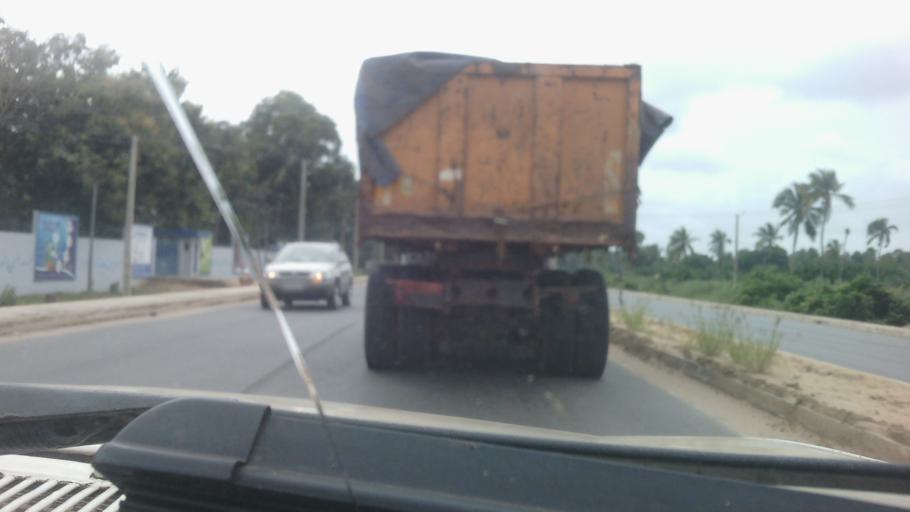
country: BJ
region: Atlantique
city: Hevie
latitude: 6.3839
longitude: 2.1933
